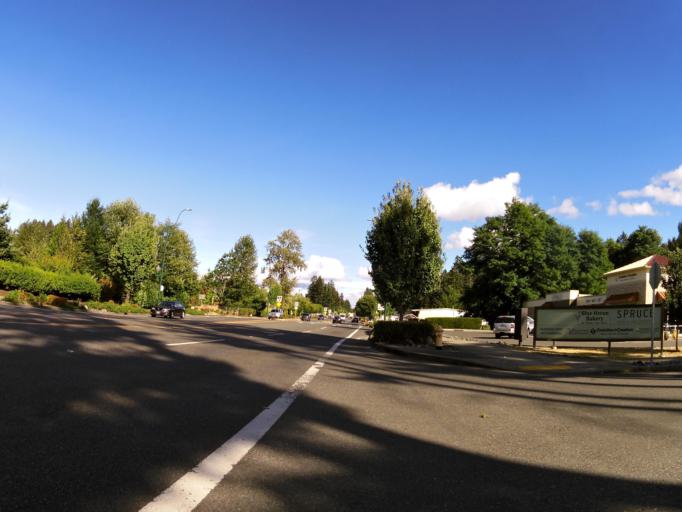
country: US
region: Washington
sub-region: Thurston County
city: Olympia
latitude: 47.0470
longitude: -122.9586
